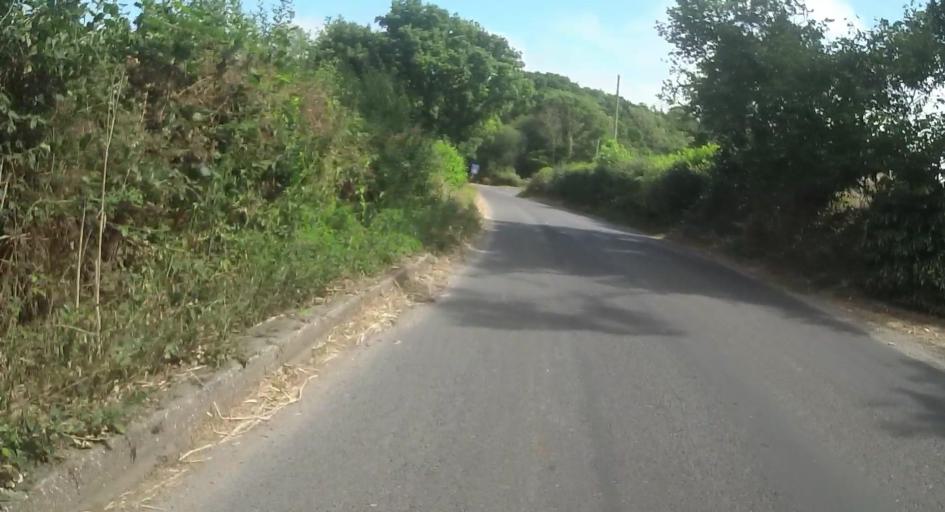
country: GB
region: England
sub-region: Dorset
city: Bovington Camp
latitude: 50.6916
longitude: -2.2694
